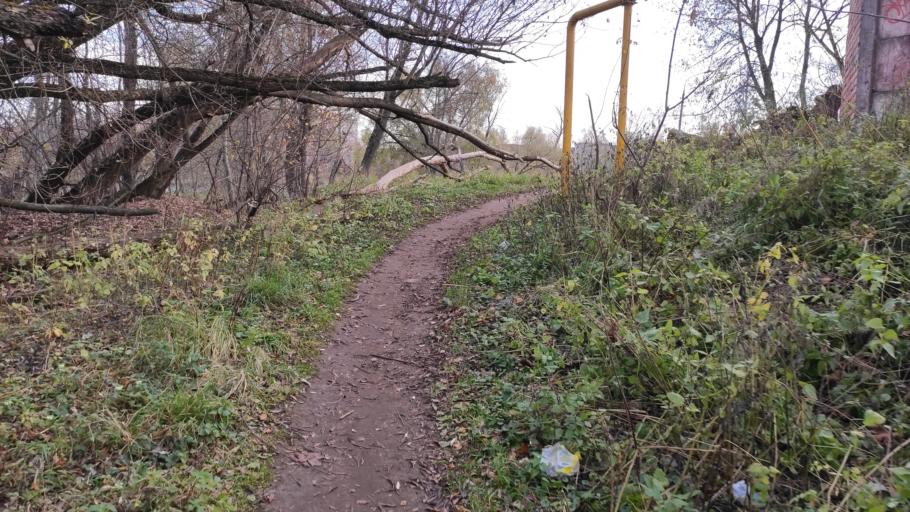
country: RU
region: Moskovskaya
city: Noginsk
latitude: 55.8731
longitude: 38.4589
